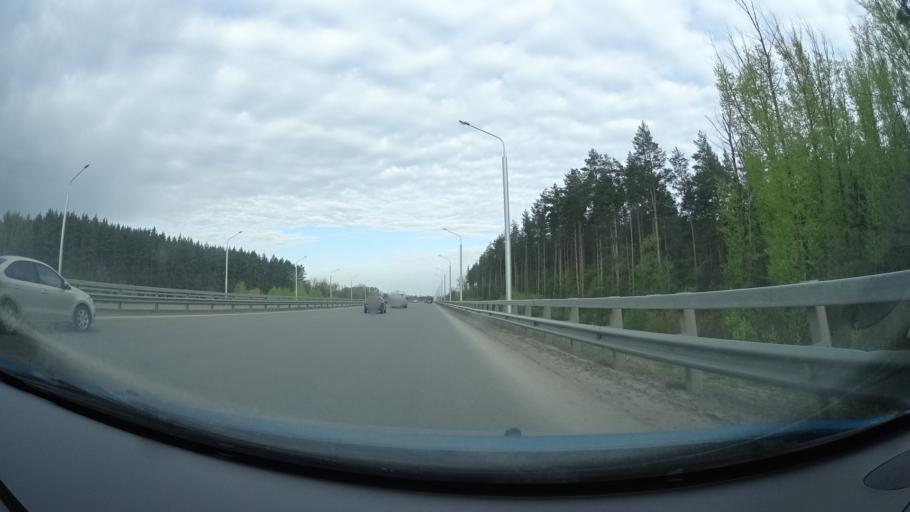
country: RU
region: Bashkortostan
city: Ufa
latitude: 54.7781
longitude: 55.9348
